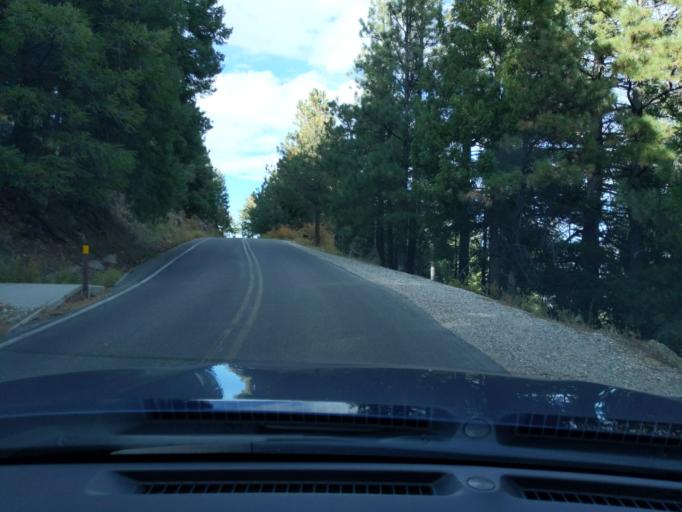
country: US
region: Arizona
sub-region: Pima County
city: Catalina
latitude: 32.4506
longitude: -110.7826
